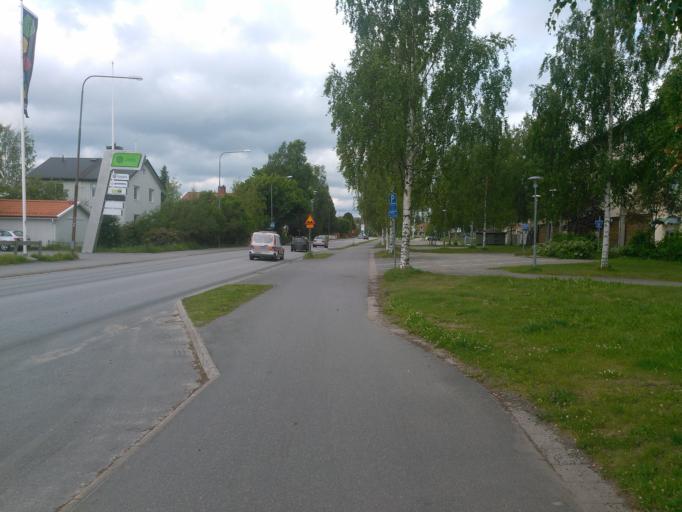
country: SE
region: Vaesterbotten
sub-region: Umea Kommun
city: Umea
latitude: 63.8295
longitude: 20.2839
